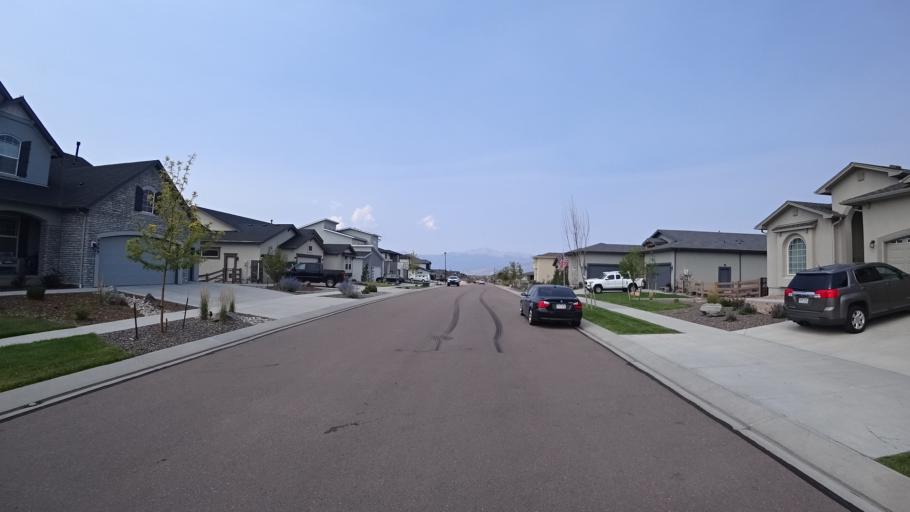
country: US
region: Colorado
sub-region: El Paso County
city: Black Forest
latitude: 38.9712
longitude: -104.7209
